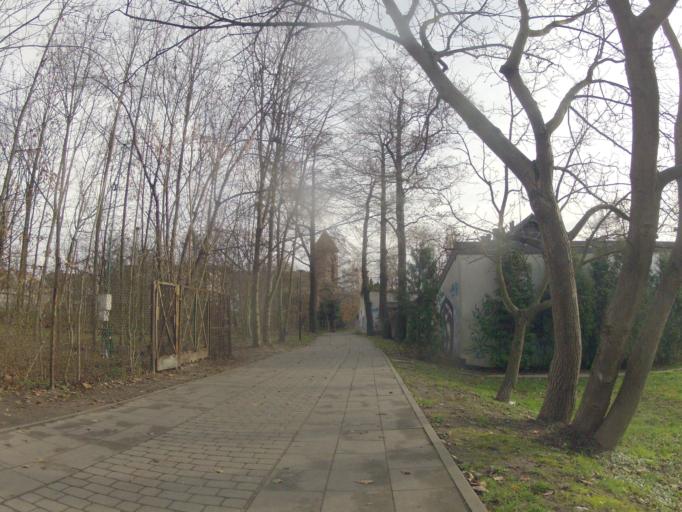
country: PL
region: Lesser Poland Voivodeship
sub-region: Krakow
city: Krakow
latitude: 50.0746
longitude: 19.8935
